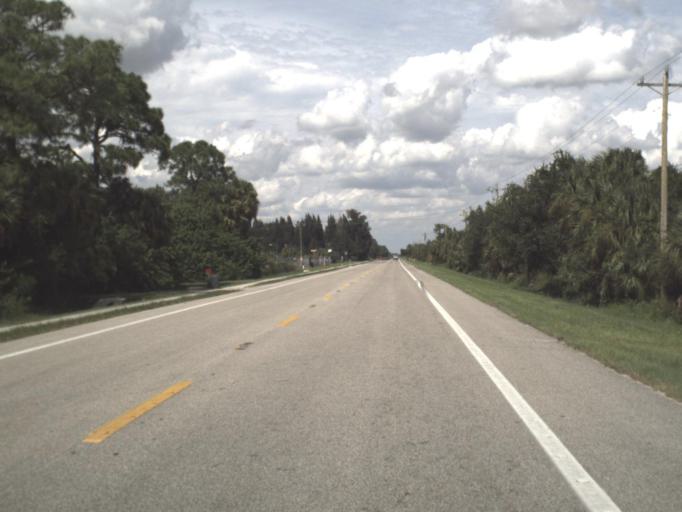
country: US
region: Florida
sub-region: Collier County
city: Immokalee
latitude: 26.5540
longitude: -81.4358
